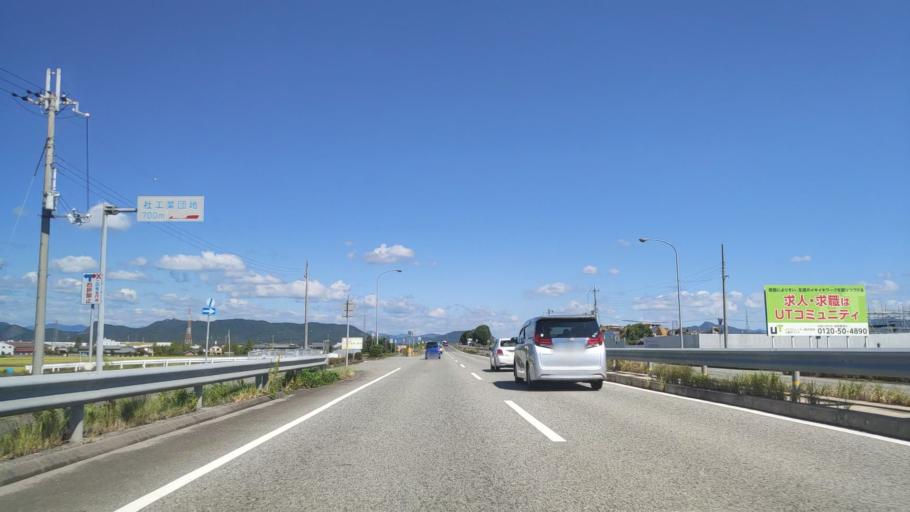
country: JP
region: Hyogo
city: Yashiro
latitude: 34.9013
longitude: 134.9520
